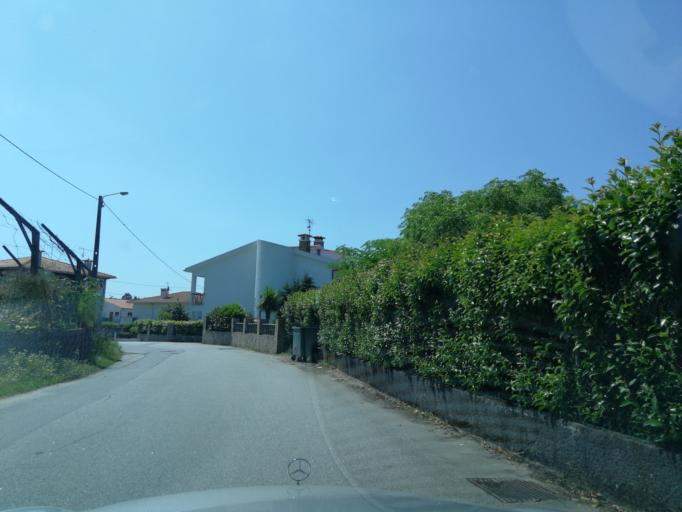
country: PT
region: Braga
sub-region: Braga
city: Adaufe
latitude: 41.5561
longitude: -8.3486
